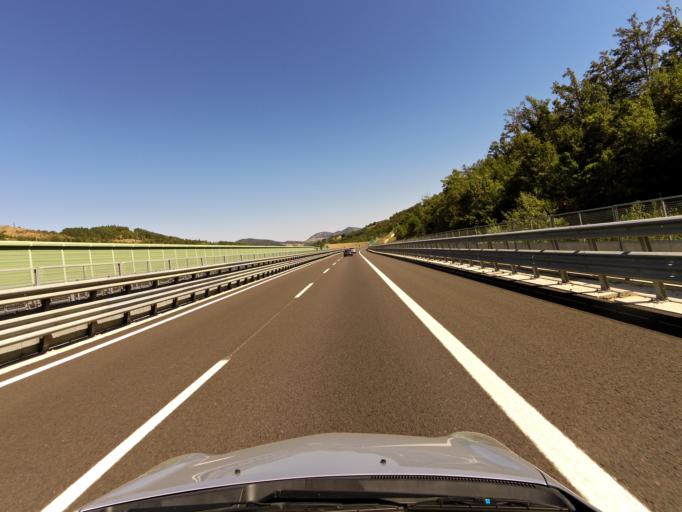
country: IT
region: Emilia-Romagna
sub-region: Provincia di Bologna
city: Grizzana
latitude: 44.2354
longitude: 11.1849
